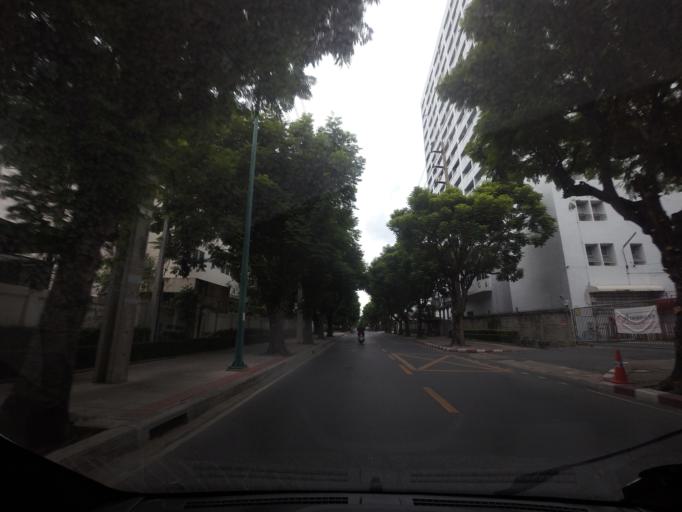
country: TH
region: Bangkok
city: Ratchathewi
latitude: 13.7621
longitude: 100.5358
